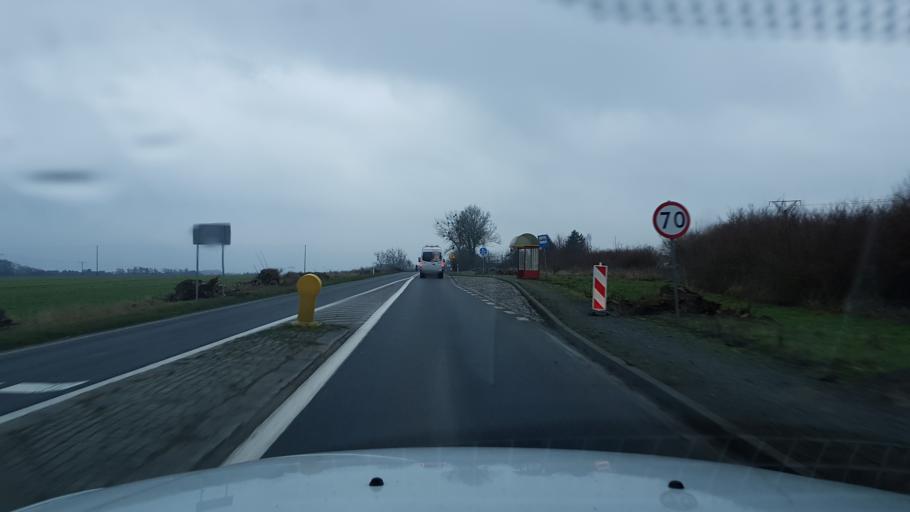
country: PL
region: West Pomeranian Voivodeship
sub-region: Powiat gryficki
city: Gryfice
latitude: 53.8719
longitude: 15.2156
